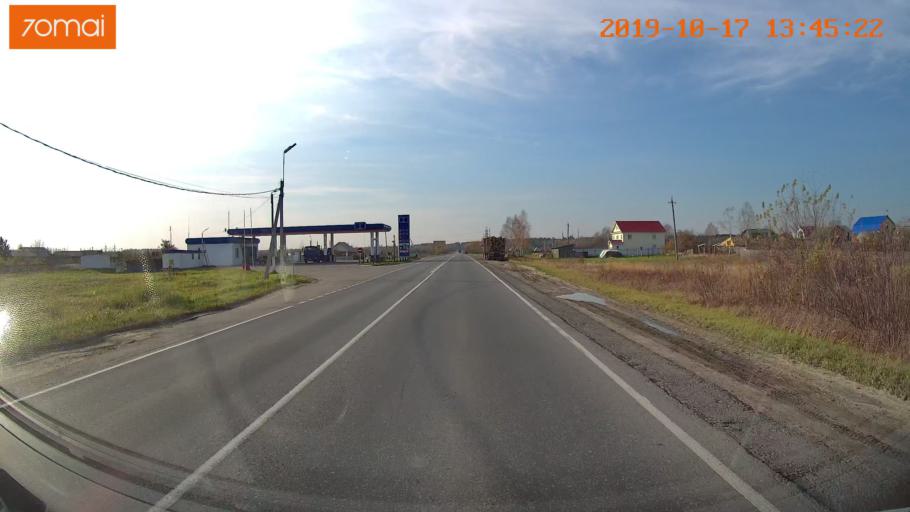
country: RU
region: Rjazan
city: Tuma
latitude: 55.1469
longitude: 40.5145
